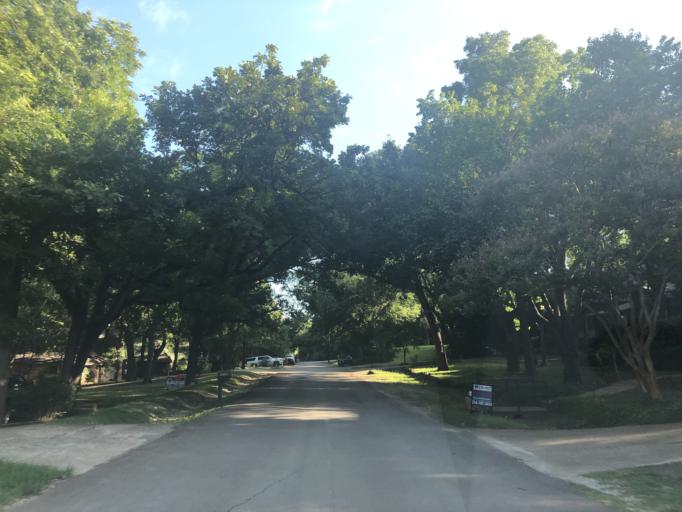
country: US
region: Texas
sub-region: Dallas County
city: Duncanville
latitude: 32.6710
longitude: -96.9221
